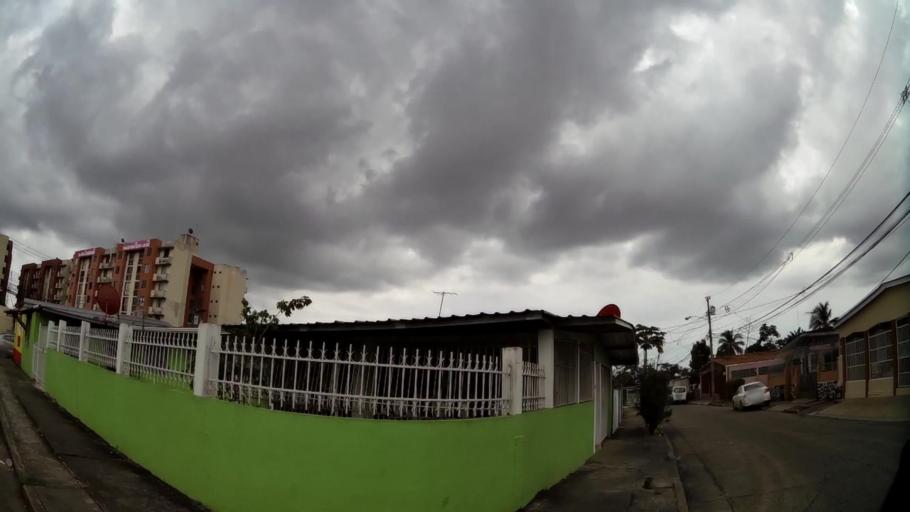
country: PA
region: Panama
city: Tocumen
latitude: 9.0628
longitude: -79.4178
